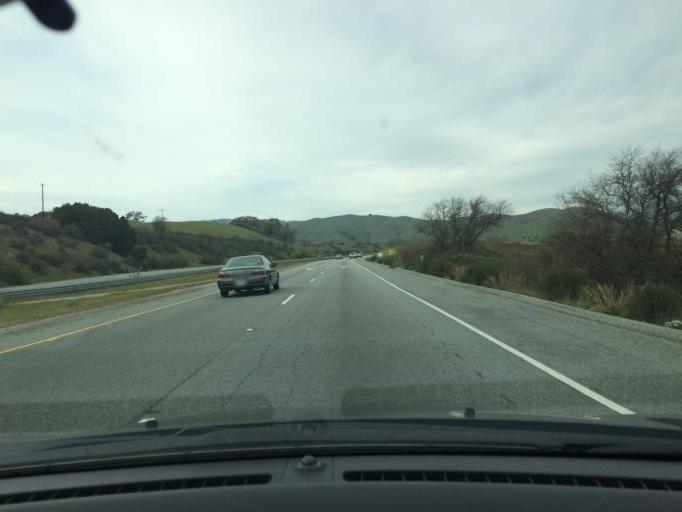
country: US
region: California
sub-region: Santa Clara County
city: Gilroy
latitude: 36.9320
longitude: -121.5498
